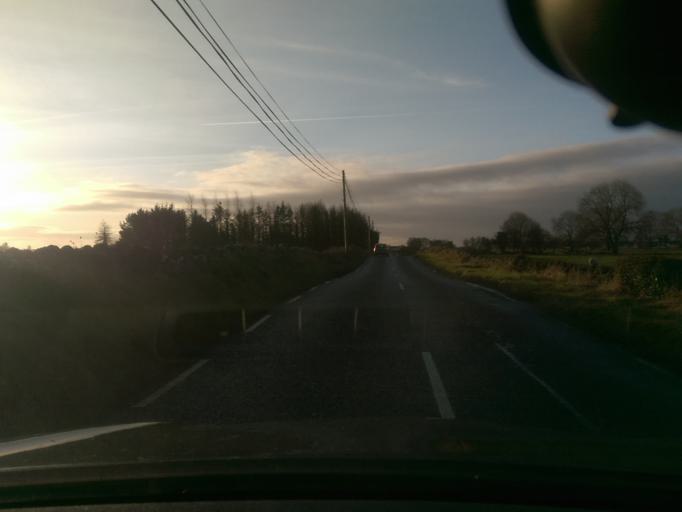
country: IE
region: Connaught
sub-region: County Galway
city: Athenry
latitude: 53.3564
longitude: -8.7052
